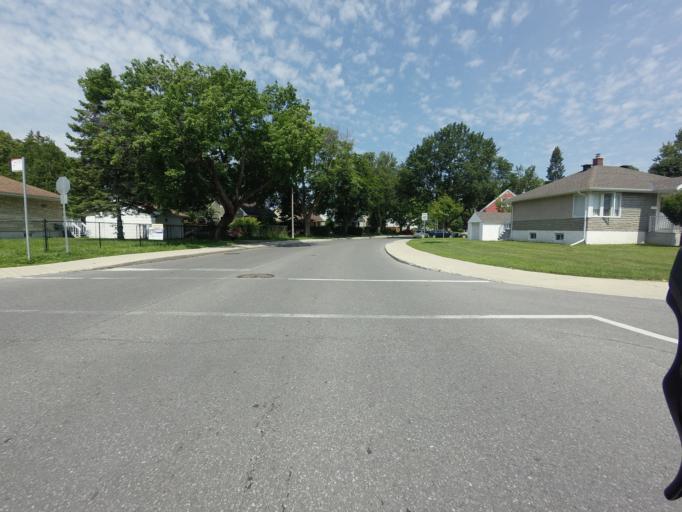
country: CA
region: Ontario
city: Ottawa
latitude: 45.3828
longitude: -75.7293
